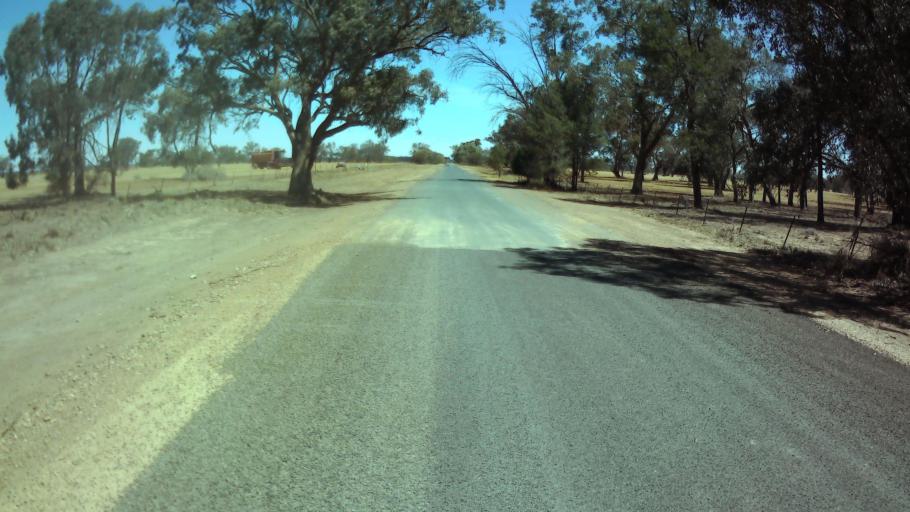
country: AU
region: New South Wales
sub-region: Weddin
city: Grenfell
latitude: -33.8443
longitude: 147.6967
